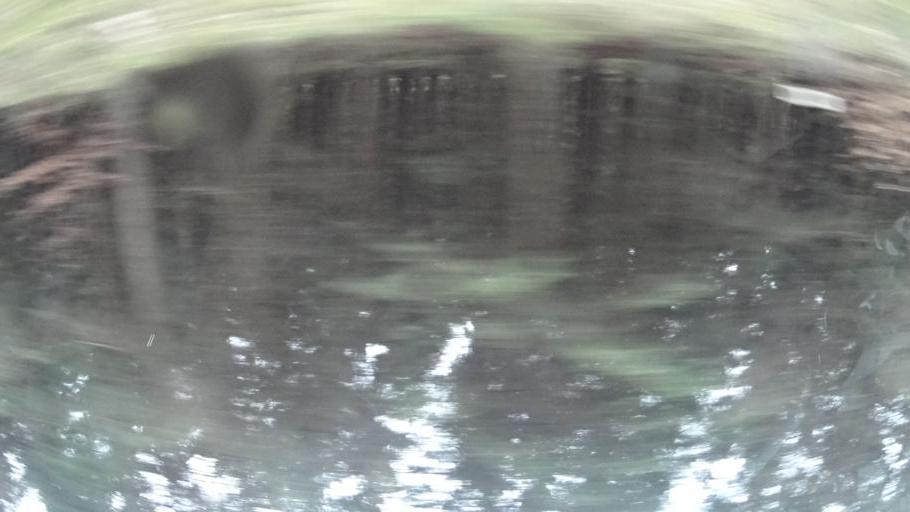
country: DE
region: Rheinland-Pfalz
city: Oberheimbach
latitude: 49.9845
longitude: 7.7909
